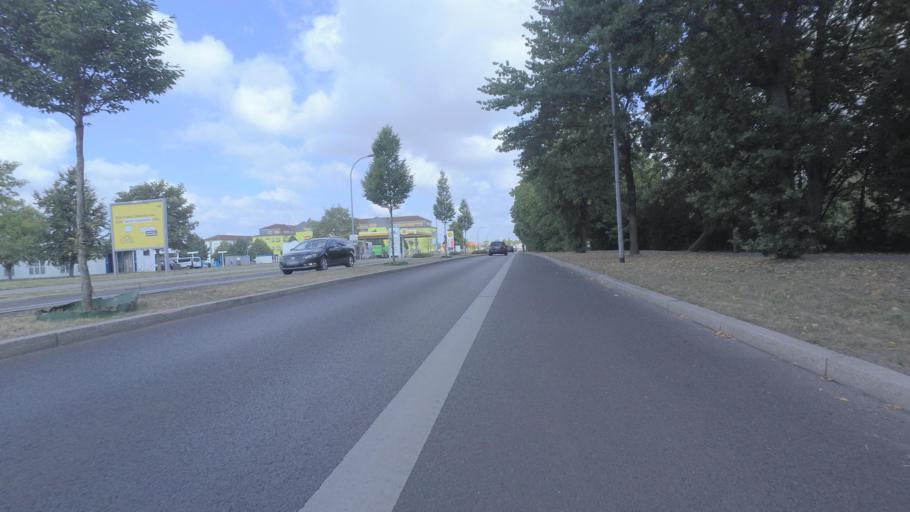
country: DE
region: Brandenburg
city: Neuruppin
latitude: 52.9177
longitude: 12.7903
